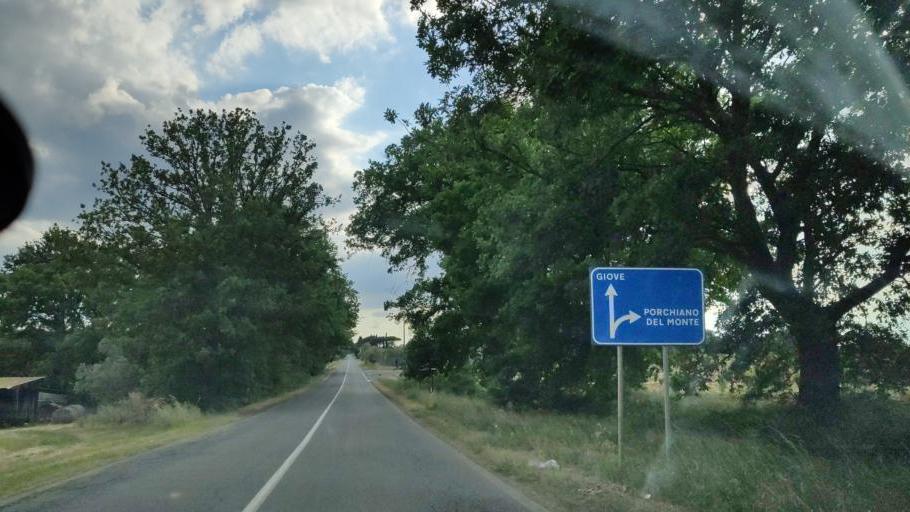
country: IT
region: Umbria
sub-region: Provincia di Terni
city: Penna in Teverina
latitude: 42.5151
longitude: 12.3608
